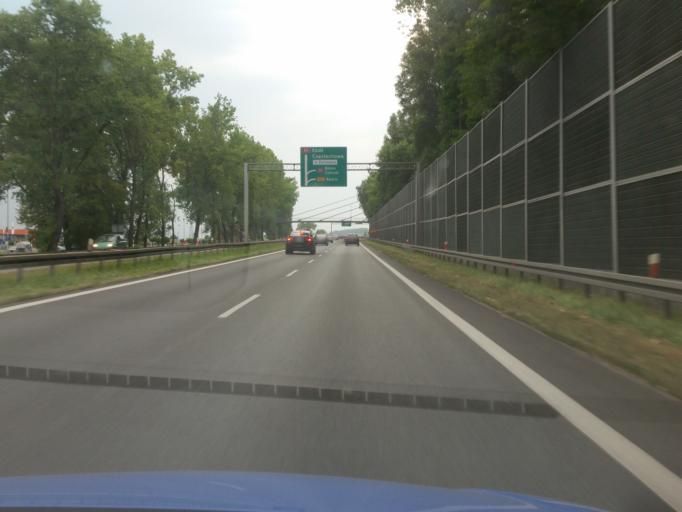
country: PL
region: Silesian Voivodeship
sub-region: Powiat bedzinski
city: Bedzin
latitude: 50.3178
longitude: 19.1088
